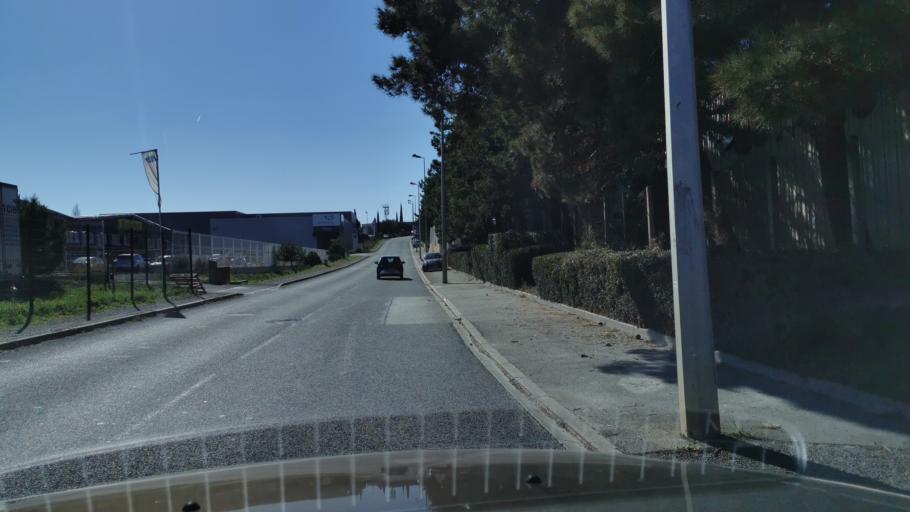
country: FR
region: Languedoc-Roussillon
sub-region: Departement de l'Aude
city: Narbonne
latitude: 43.1550
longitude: 2.9789
